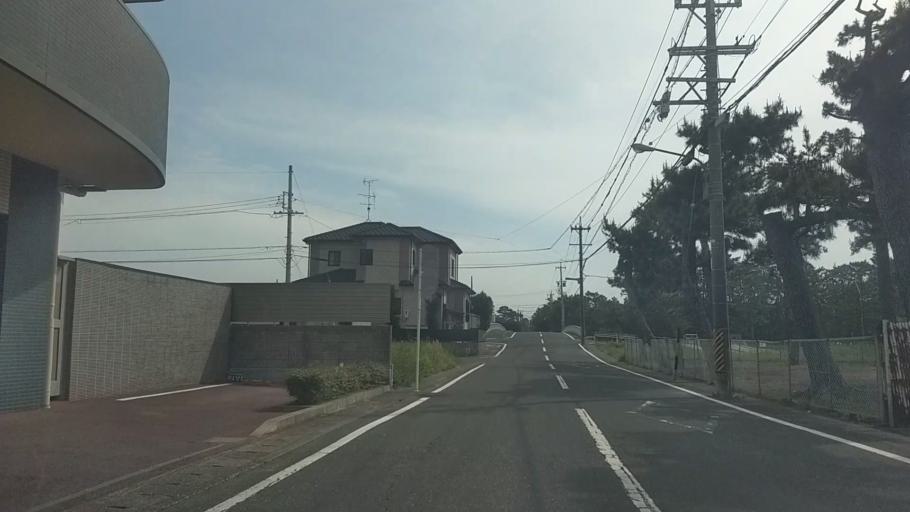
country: JP
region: Shizuoka
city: Kosai-shi
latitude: 34.6975
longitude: 137.5988
